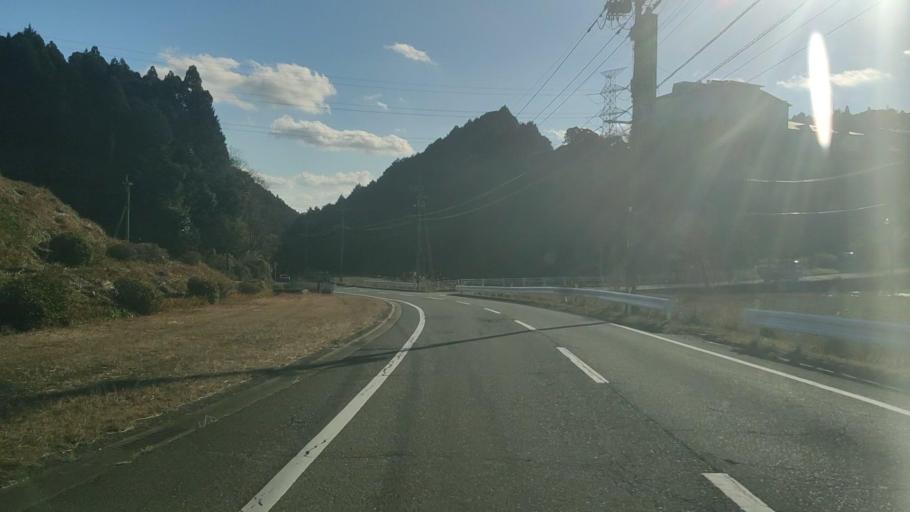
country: JP
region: Saga Prefecture
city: Kanzakimachi-kanzaki
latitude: 33.3996
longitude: 130.2717
